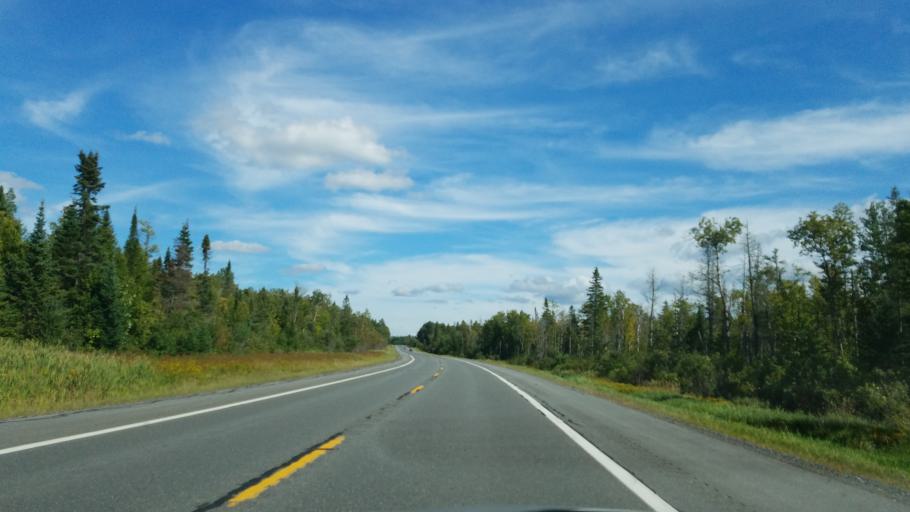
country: US
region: Michigan
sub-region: Baraga County
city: L'Anse
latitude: 46.5817
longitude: -88.4657
